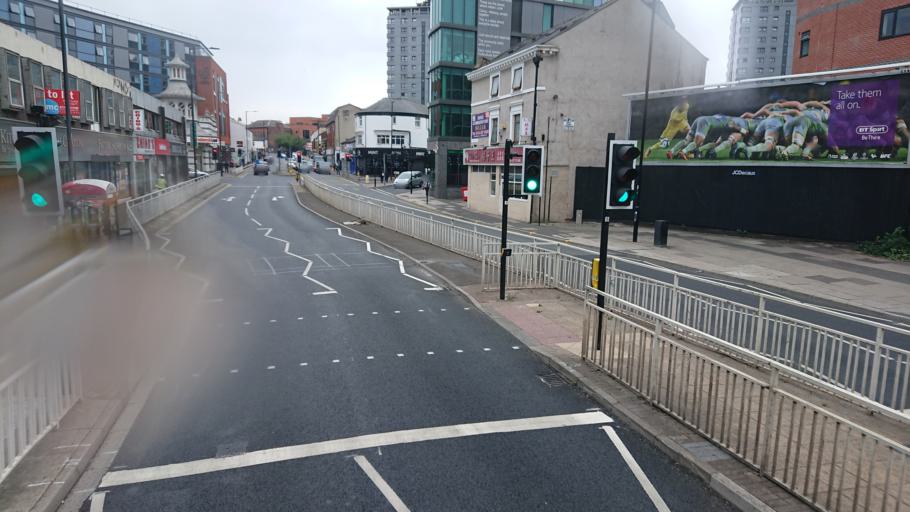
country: GB
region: England
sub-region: Sheffield
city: Sheffield
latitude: 53.3729
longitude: -1.4767
